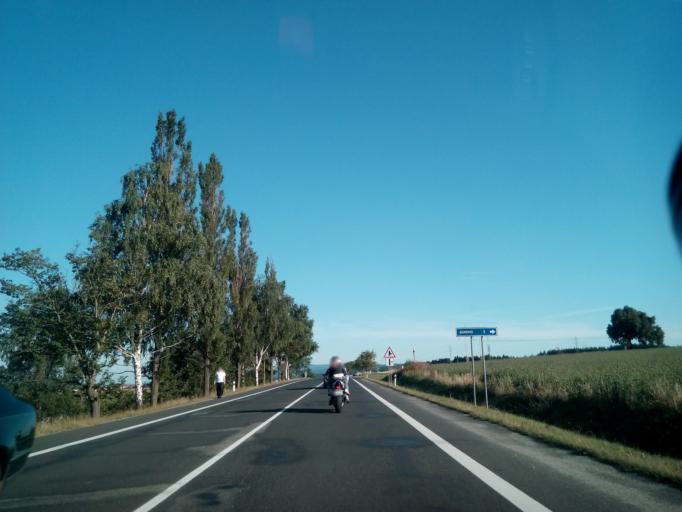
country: SK
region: Presovsky
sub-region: Okres Poprad
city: Poprad
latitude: 49.0414
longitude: 20.3283
